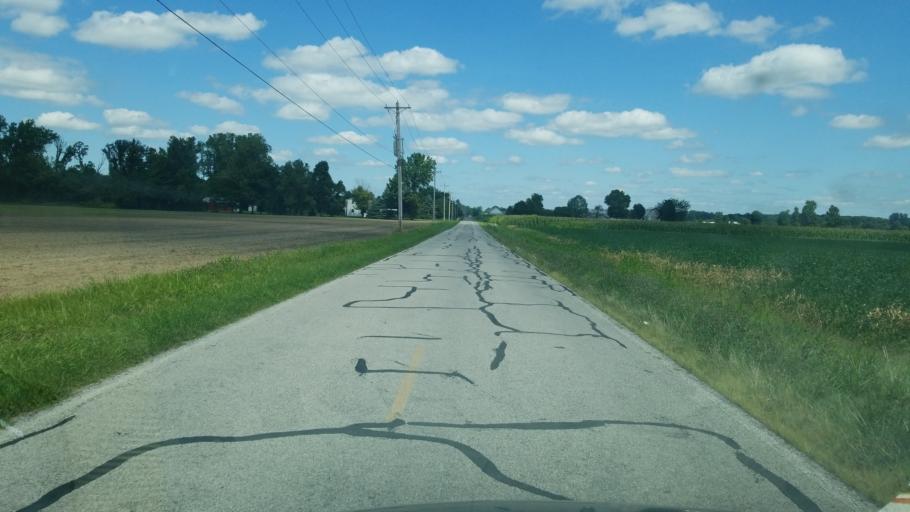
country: US
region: Ohio
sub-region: Henry County
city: Liberty Center
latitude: 41.5036
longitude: -83.9413
